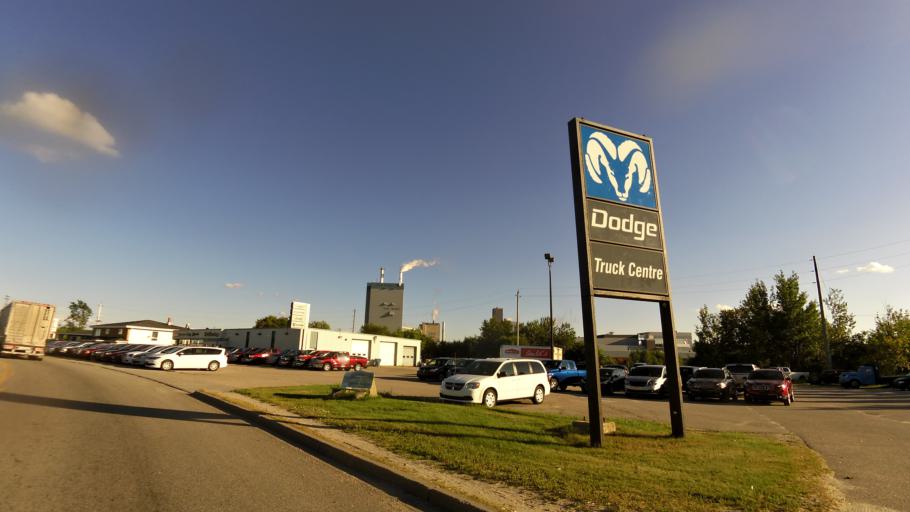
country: CA
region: Ontario
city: Dryden
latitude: 49.7877
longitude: -92.8469
